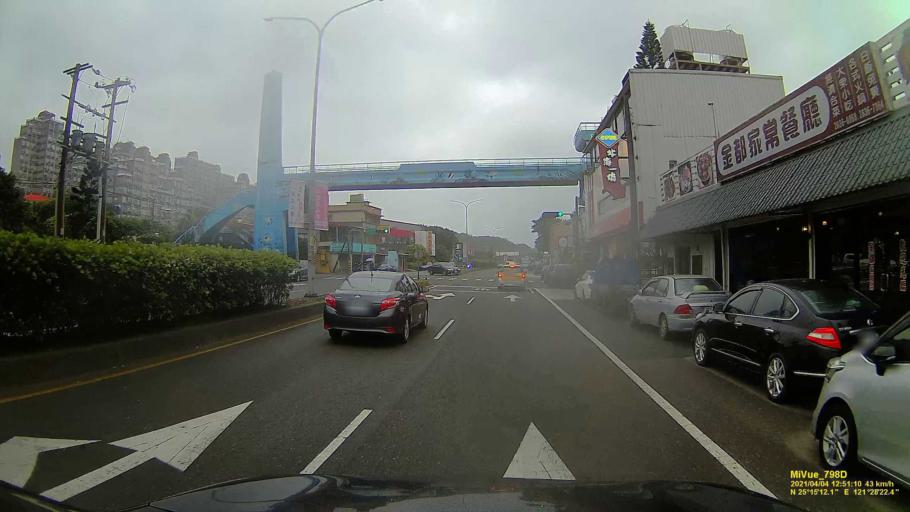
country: TW
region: Taipei
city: Taipei
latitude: 25.2532
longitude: 121.4727
